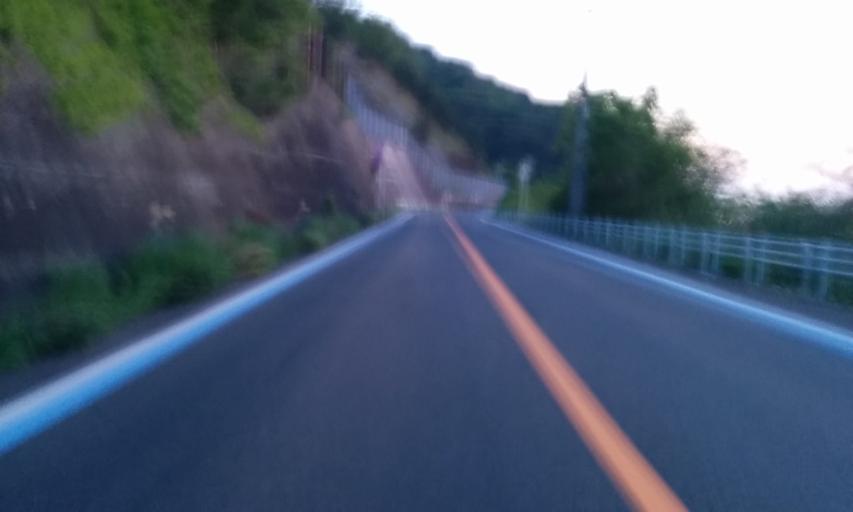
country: JP
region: Ehime
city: Ozu
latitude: 33.5967
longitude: 132.4613
